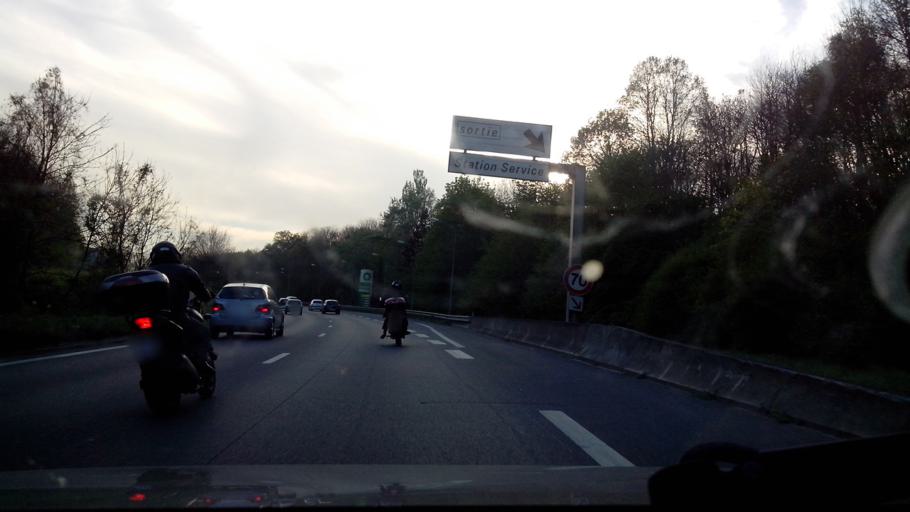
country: FR
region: Ile-de-France
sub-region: Departement de l'Essonne
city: Vauhallan
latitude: 48.7502
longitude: 2.2030
